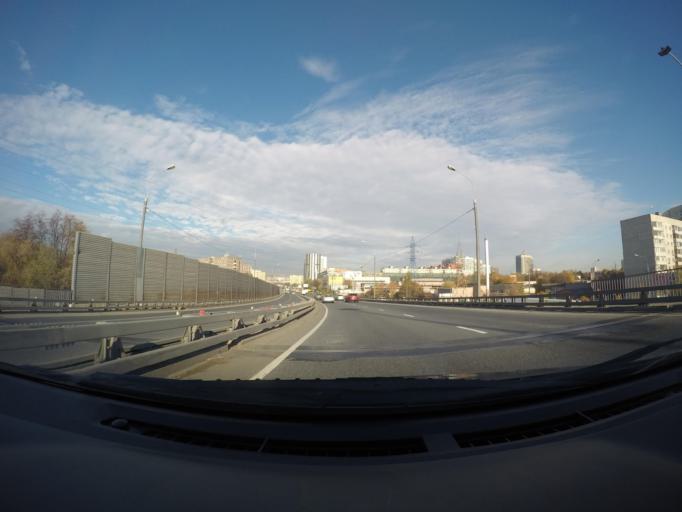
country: RU
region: Moskovskaya
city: Druzhba
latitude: 55.9109
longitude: 37.7767
